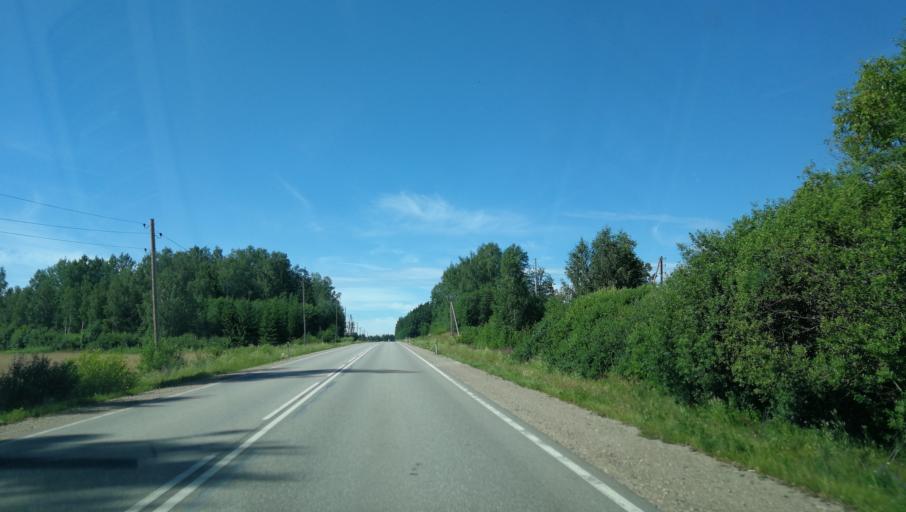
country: LV
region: Gulbenes Rajons
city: Gulbene
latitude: 57.1388
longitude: 26.7091
